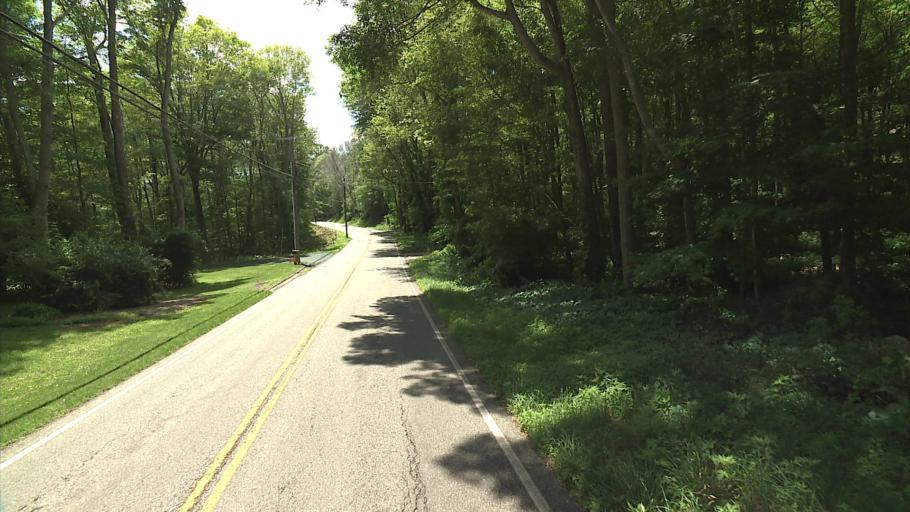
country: US
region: Connecticut
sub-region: New London County
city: Old Mystic
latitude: 41.4485
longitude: -71.9060
